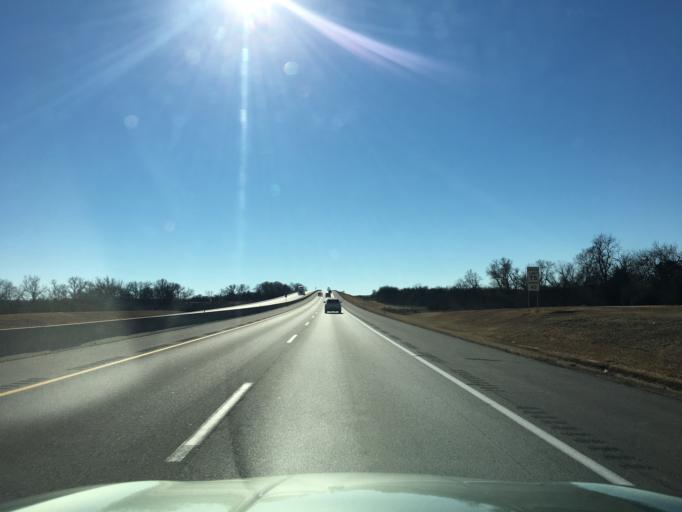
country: US
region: Kansas
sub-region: Sumner County
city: Belle Plaine
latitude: 37.3570
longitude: -97.3222
